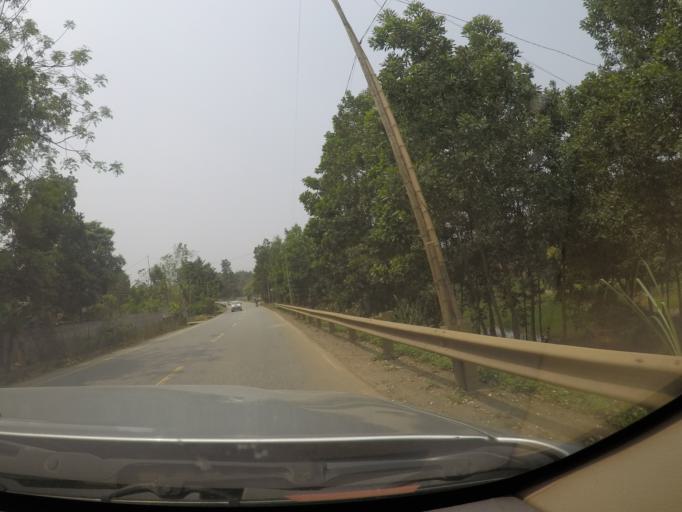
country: VN
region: Thanh Hoa
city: Thi Tran Ngoc Lac
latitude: 20.1364
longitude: 105.4177
